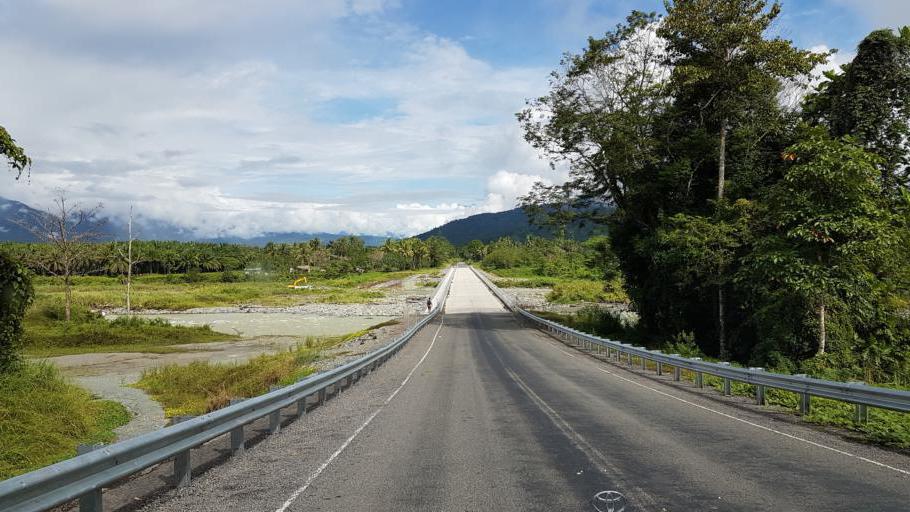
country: PG
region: Northern Province
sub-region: Sohe
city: Kokoda
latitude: -8.9053
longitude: 147.9831
